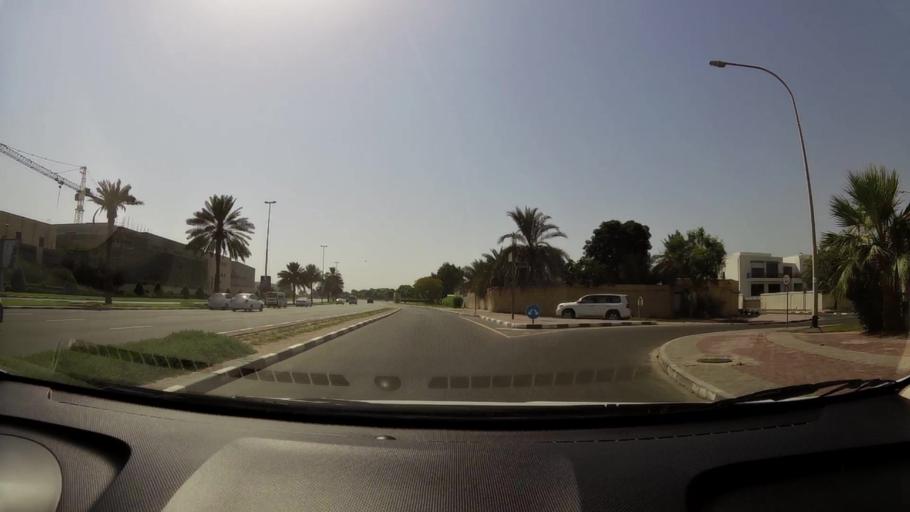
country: AE
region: Ash Shariqah
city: Sharjah
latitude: 25.2665
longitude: 55.3671
